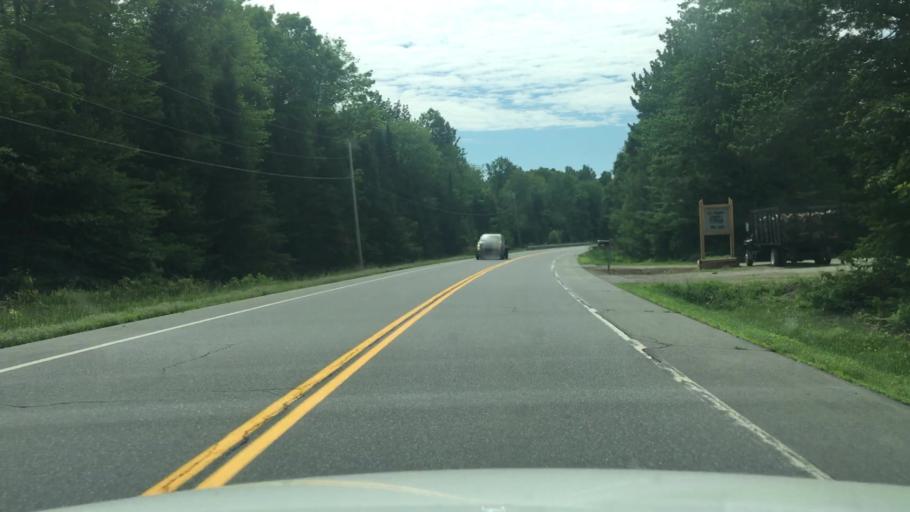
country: US
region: Maine
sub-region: Waldo County
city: Troy
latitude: 44.5994
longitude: -69.2876
